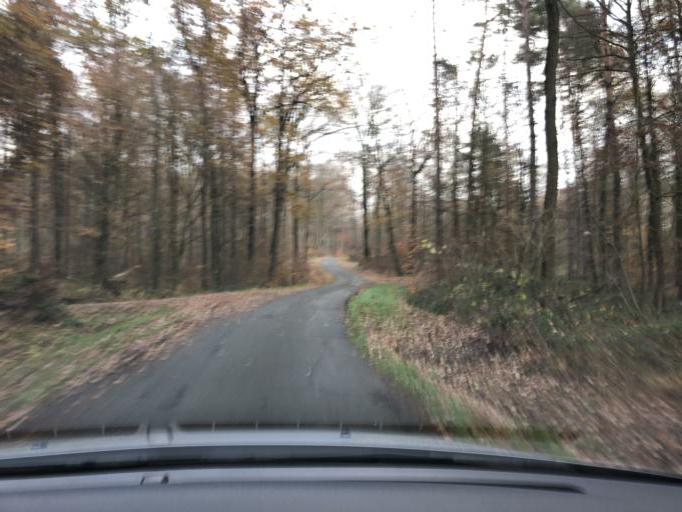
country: DE
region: Saxony
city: Mutzschen
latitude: 51.2820
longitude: 12.9133
